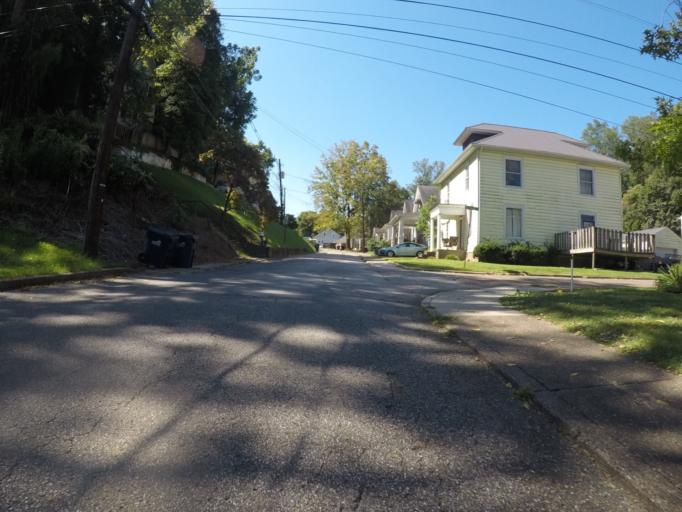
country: US
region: Kentucky
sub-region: Boyd County
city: Ashland
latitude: 38.4734
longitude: -82.6448
